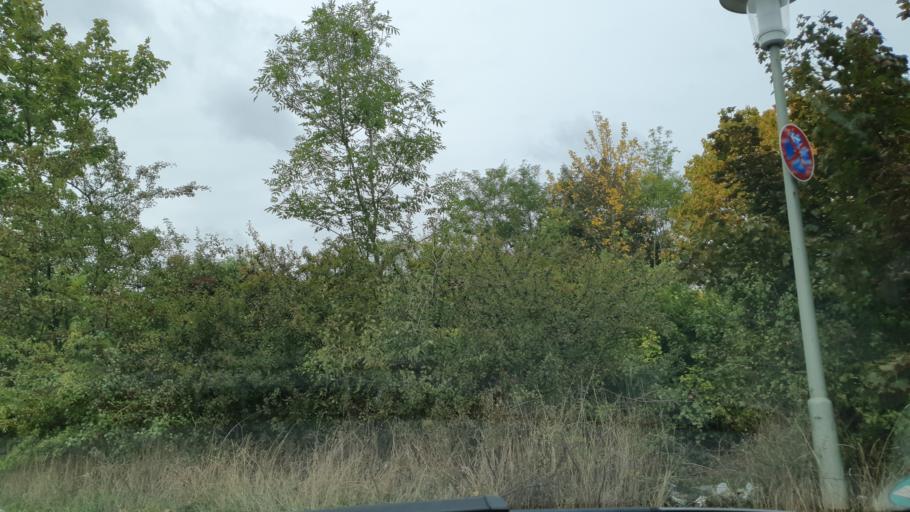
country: DE
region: Rheinland-Pfalz
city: Kaiserslautern
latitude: 49.4548
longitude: 7.7909
